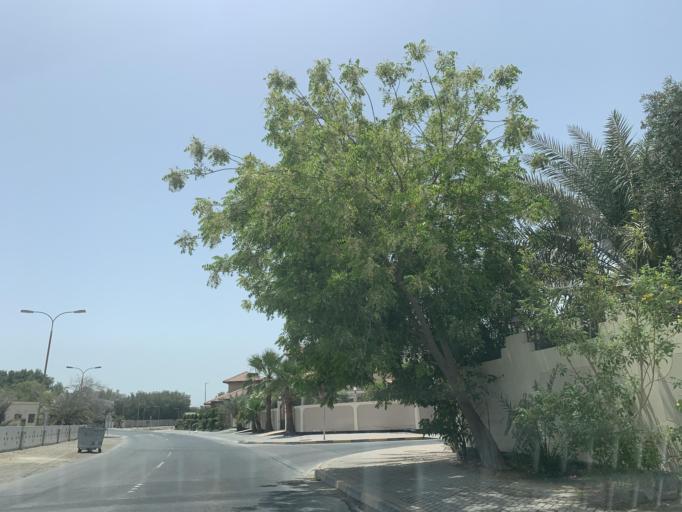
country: BH
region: Northern
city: Madinat `Isa
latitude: 26.1631
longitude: 50.5792
